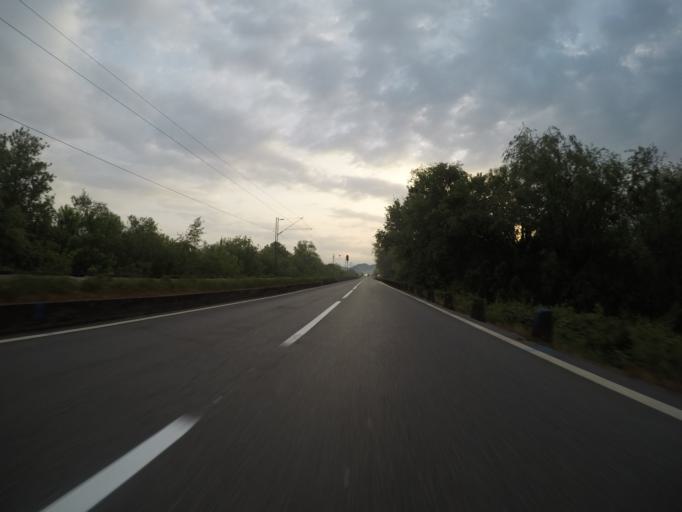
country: ME
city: Mojanovici
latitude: 42.2903
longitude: 19.1510
